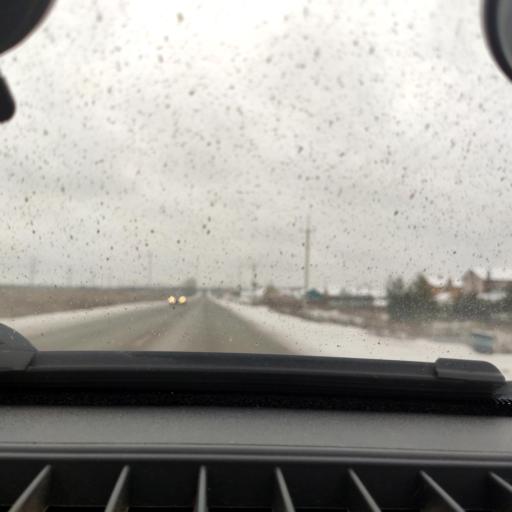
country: RU
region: Bashkortostan
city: Iglino
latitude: 54.7885
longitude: 56.2521
